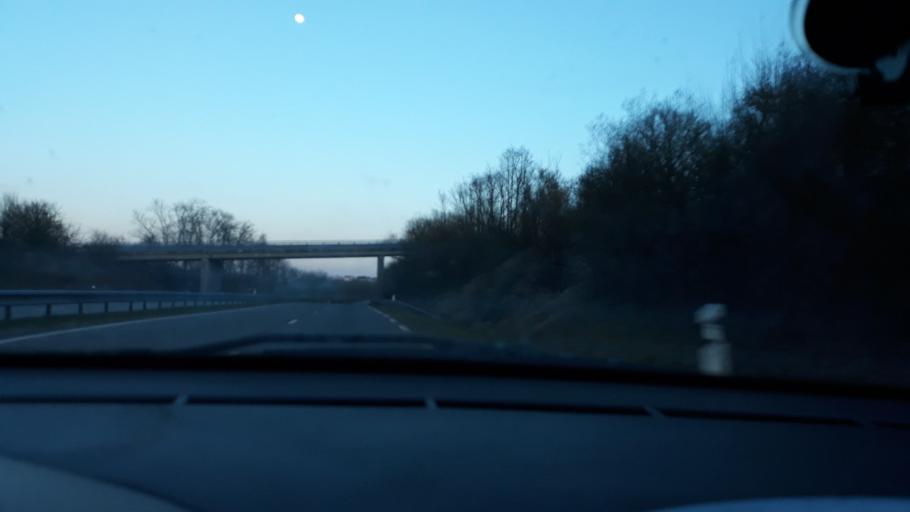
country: FR
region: Lorraine
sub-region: Departement de la Moselle
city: Kerbach
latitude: 49.1568
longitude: 6.9691
